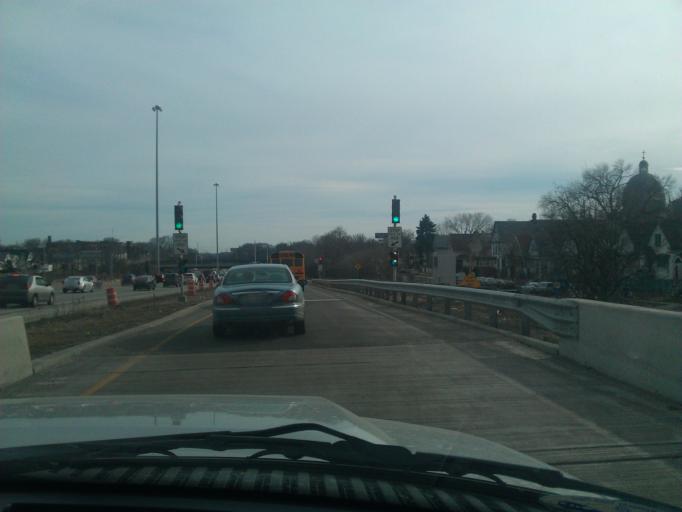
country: US
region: Wisconsin
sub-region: Milwaukee County
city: Milwaukee
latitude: 43.0062
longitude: -87.9165
